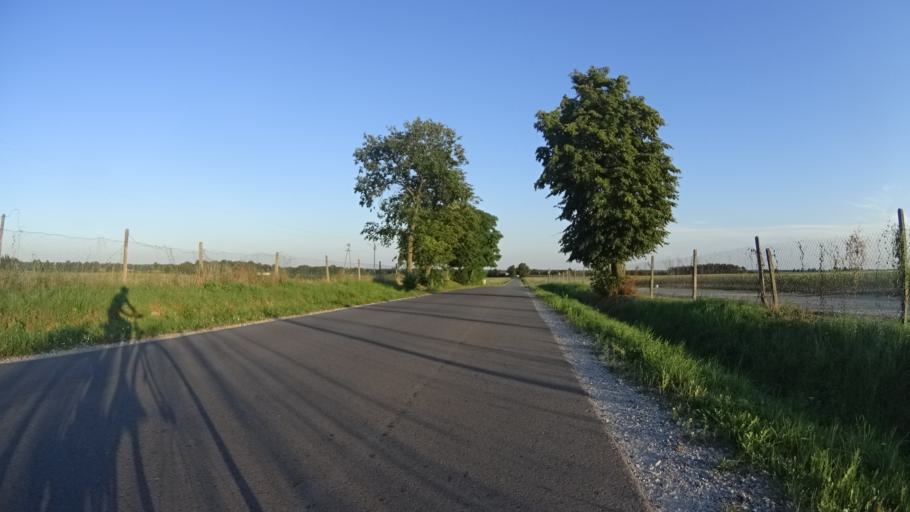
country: PL
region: Masovian Voivodeship
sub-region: Powiat grojecki
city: Goszczyn
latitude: 51.6823
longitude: 20.8250
